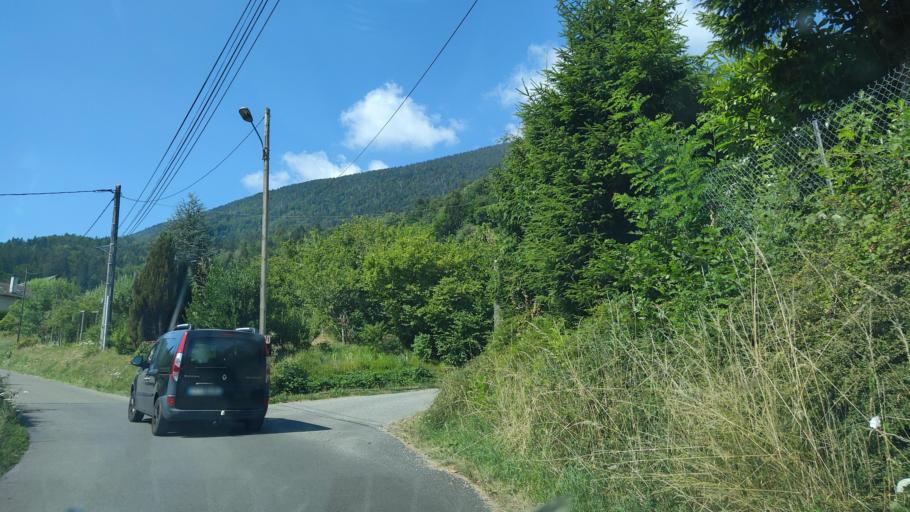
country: FR
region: Rhone-Alpes
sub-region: Departement de la Haute-Savoie
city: Saint-Jorioz
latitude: 45.8106
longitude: 6.1407
